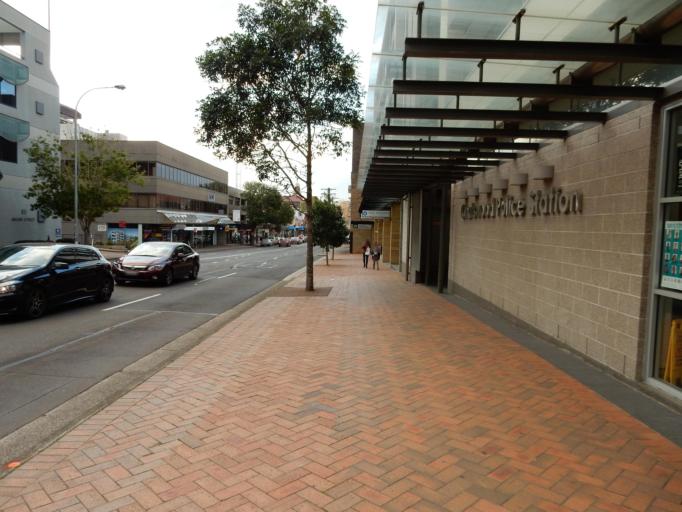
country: AU
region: New South Wales
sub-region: Willoughby
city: Chatswood
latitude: -33.7972
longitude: 151.1863
